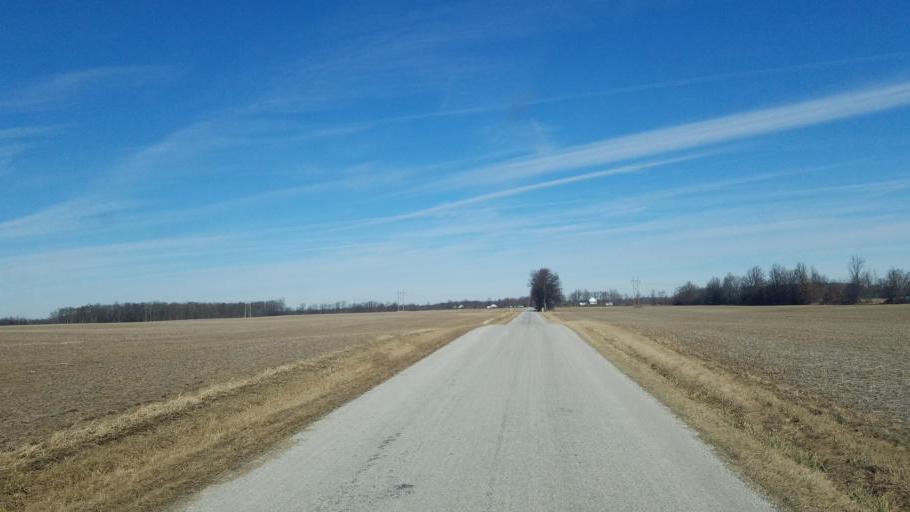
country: US
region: Ohio
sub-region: Union County
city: Richwood
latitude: 40.5708
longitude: -83.4182
